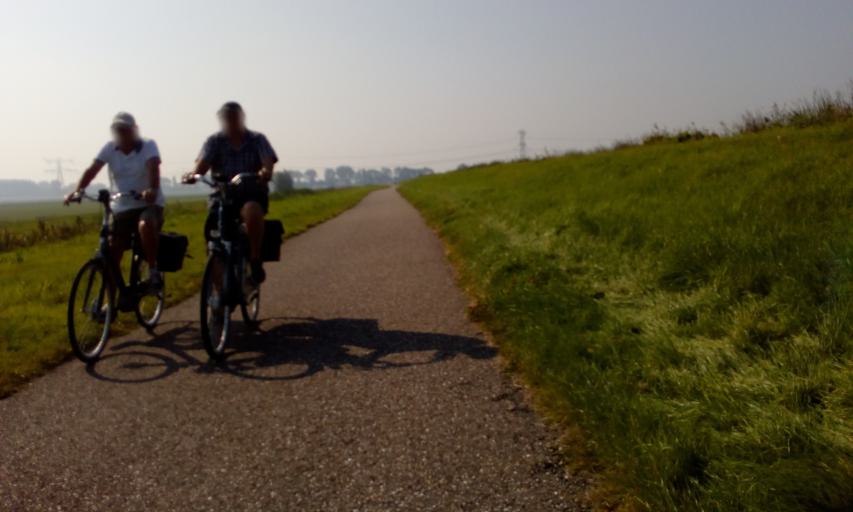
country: NL
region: South Holland
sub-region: Gemeente Lansingerland
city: Bleiswijk
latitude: 52.0381
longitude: 4.5646
